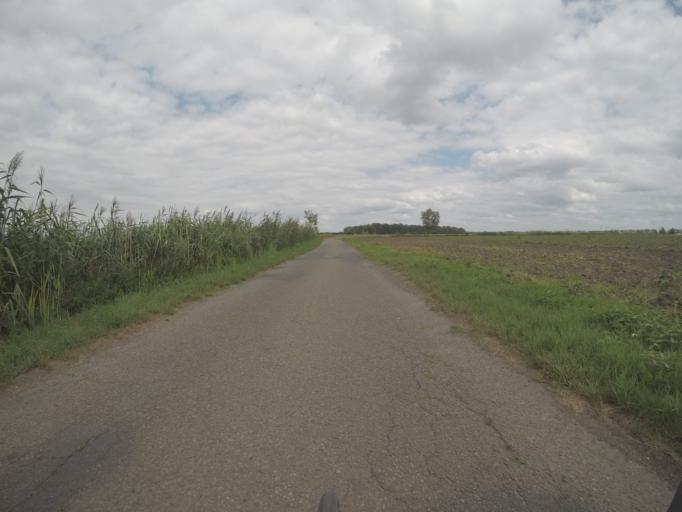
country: DE
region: Brandenburg
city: Wustermark
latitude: 52.6013
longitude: 12.9371
